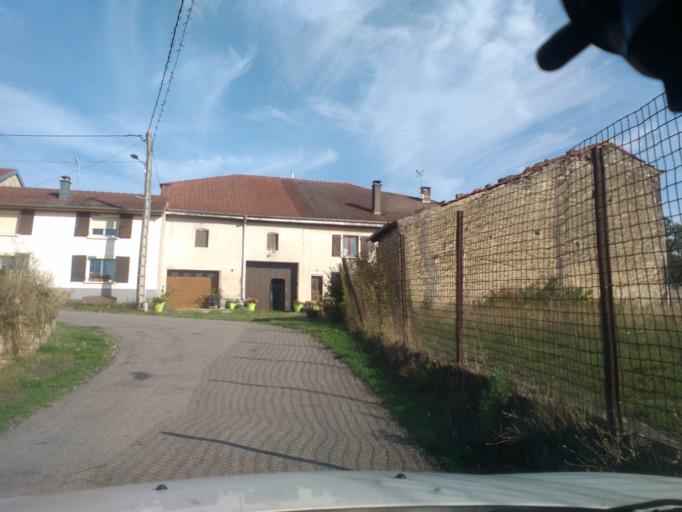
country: FR
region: Lorraine
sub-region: Departement des Vosges
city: Mirecourt
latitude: 48.2792
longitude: 6.0410
